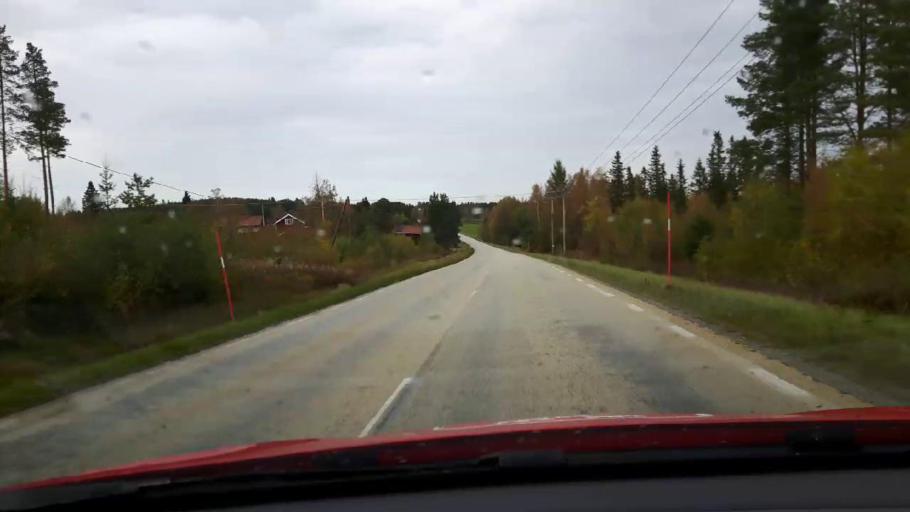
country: SE
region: Jaemtland
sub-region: Bergs Kommun
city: Hoverberg
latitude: 62.9731
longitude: 14.3487
